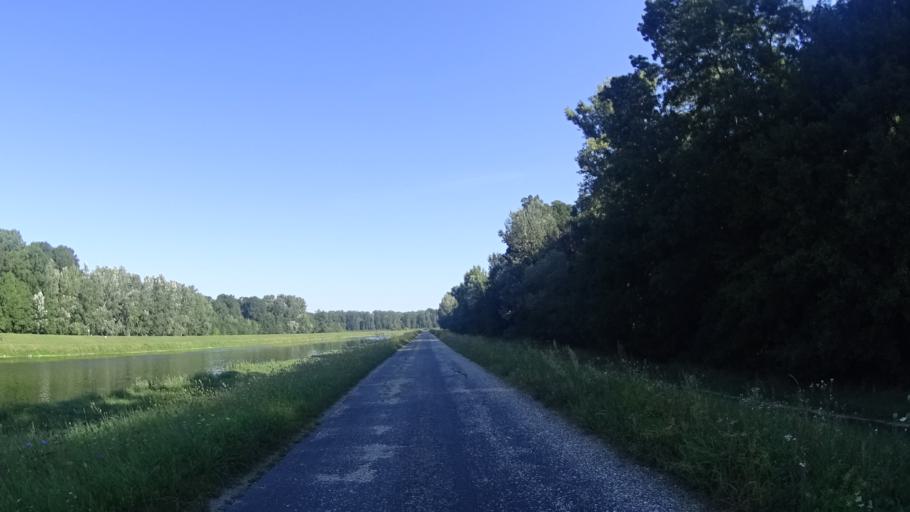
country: CZ
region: South Moravian
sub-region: Okres Breclav
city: Lanzhot
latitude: 48.7005
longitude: 16.9987
